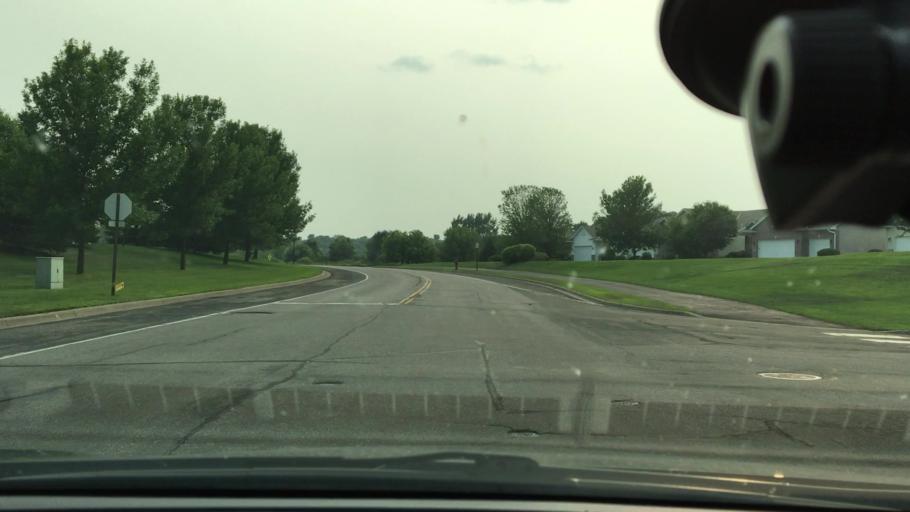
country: US
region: Minnesota
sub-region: Wright County
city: Otsego
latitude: 45.2630
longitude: -93.5753
